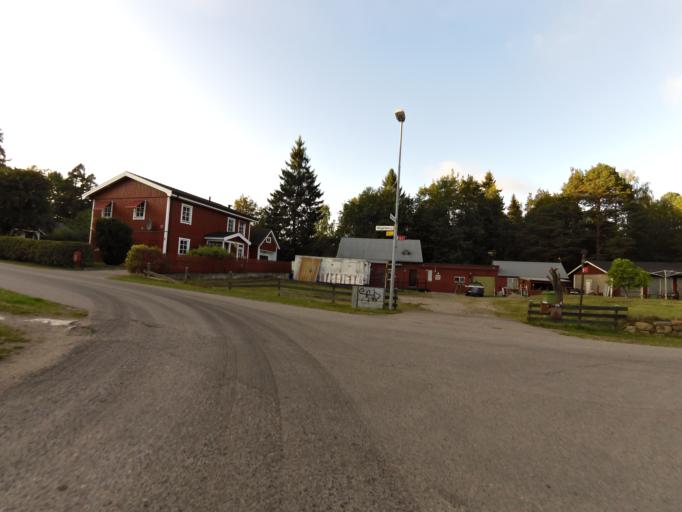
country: SE
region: Gaevleborg
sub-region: Gavle Kommun
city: Gavle
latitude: 60.6739
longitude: 17.2434
